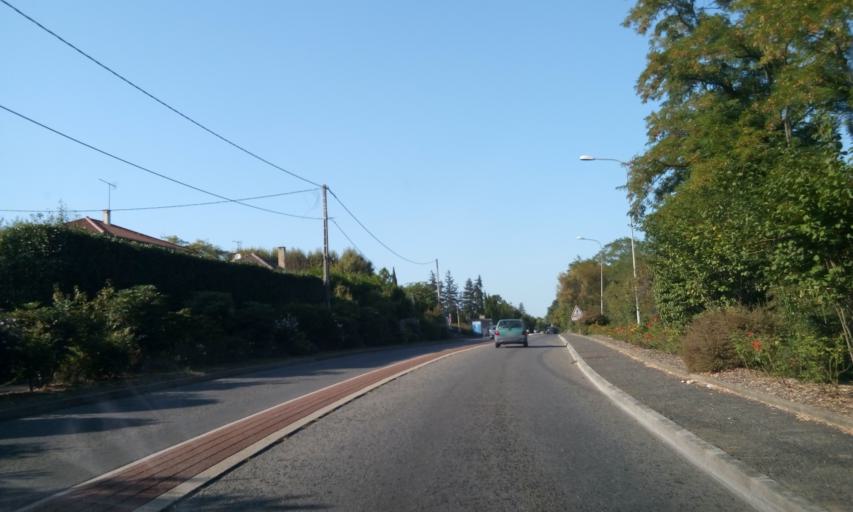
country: FR
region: Rhone-Alpes
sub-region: Departement du Rhone
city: Anse
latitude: 45.9456
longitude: 4.7143
